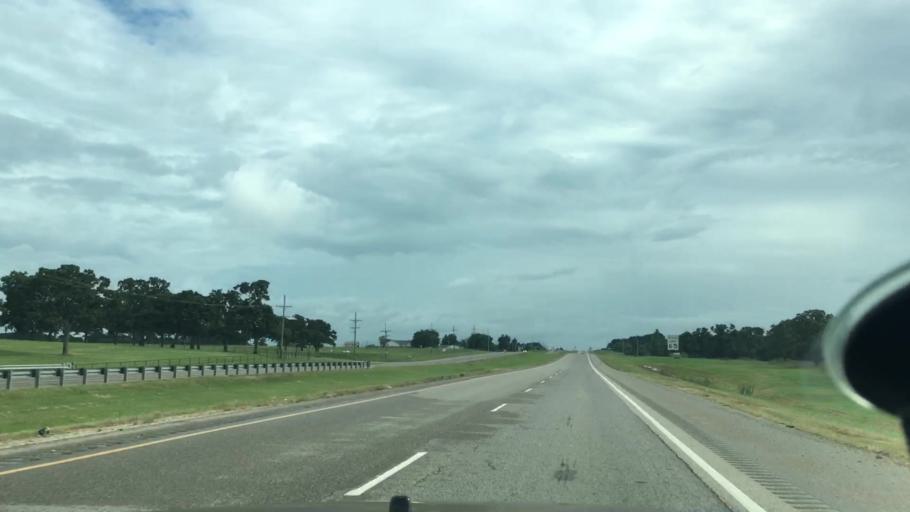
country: US
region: Oklahoma
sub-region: Lincoln County
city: Prague
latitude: 35.3598
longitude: -96.6718
